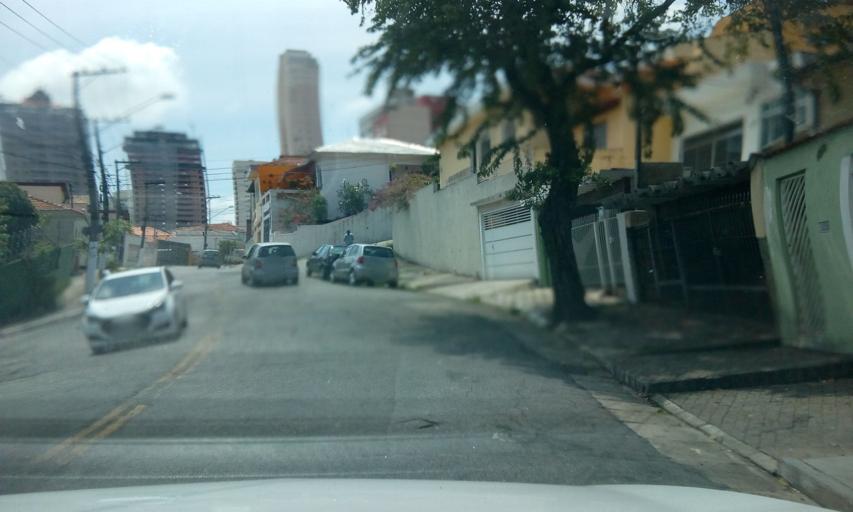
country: BR
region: Sao Paulo
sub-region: Sao Paulo
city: Sao Paulo
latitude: -23.5306
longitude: -46.7017
